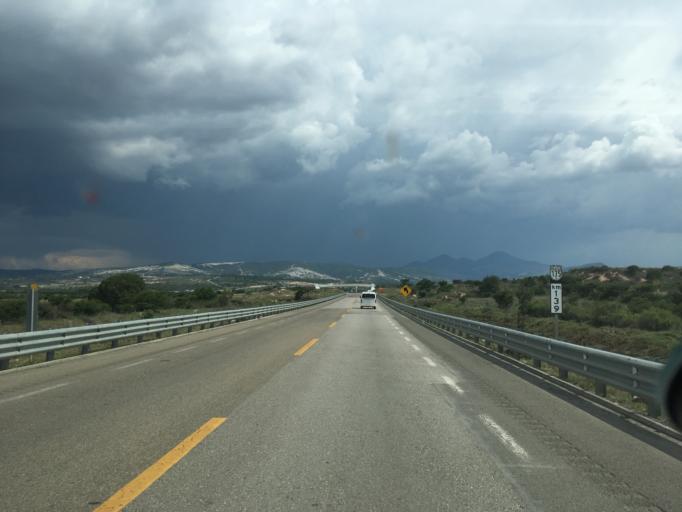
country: MX
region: Oaxaca
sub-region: Villa Tejupam de la Union
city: Villa Tejupam de la Union
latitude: 17.7514
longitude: -97.3547
